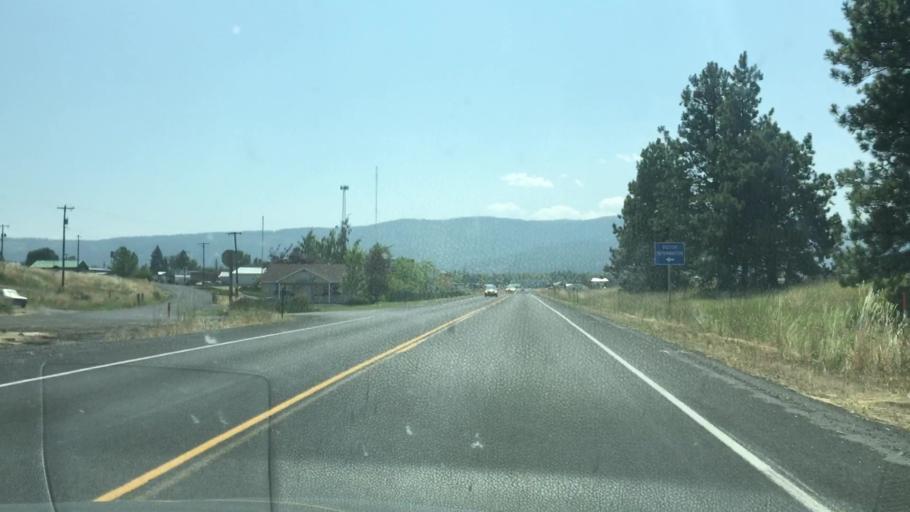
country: US
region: Idaho
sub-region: Idaho County
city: Grangeville
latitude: 45.9337
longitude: -116.1329
